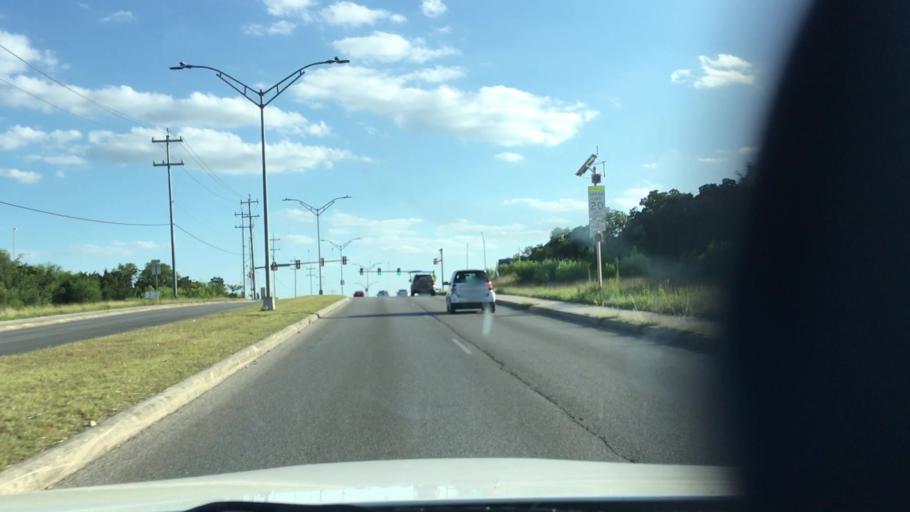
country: US
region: Texas
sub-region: Bexar County
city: Timberwood Park
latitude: 29.6593
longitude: -98.4379
